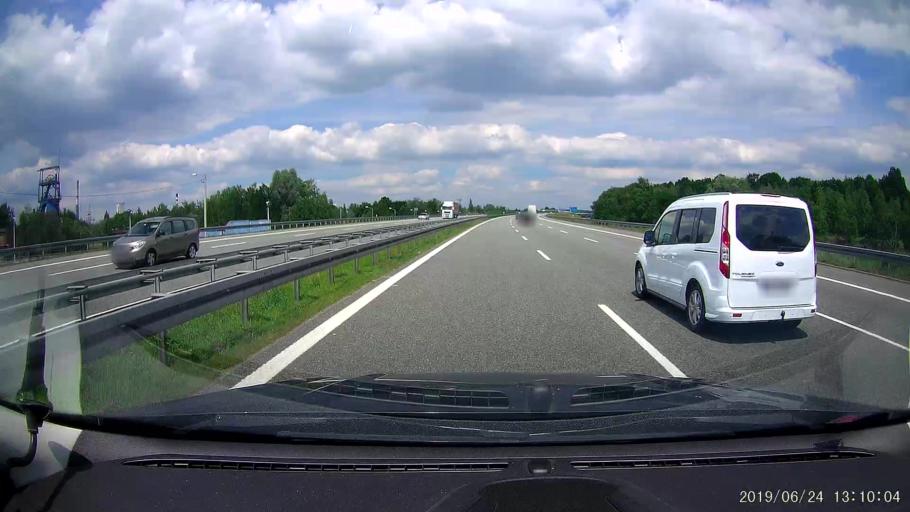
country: PL
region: Silesian Voivodeship
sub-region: Powiat gliwicki
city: Gieraltowice
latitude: 50.2113
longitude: 18.6933
